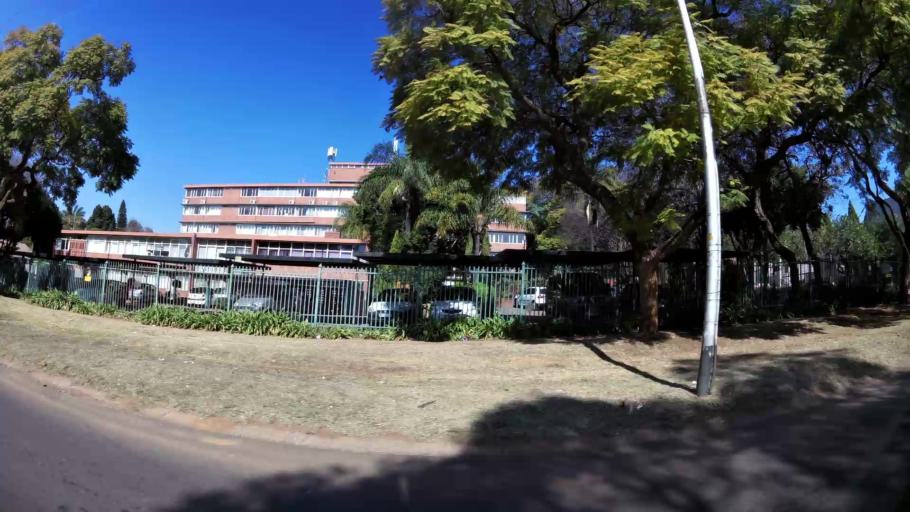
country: ZA
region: Gauteng
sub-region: City of Tshwane Metropolitan Municipality
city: Pretoria
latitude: -25.7730
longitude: 28.2267
